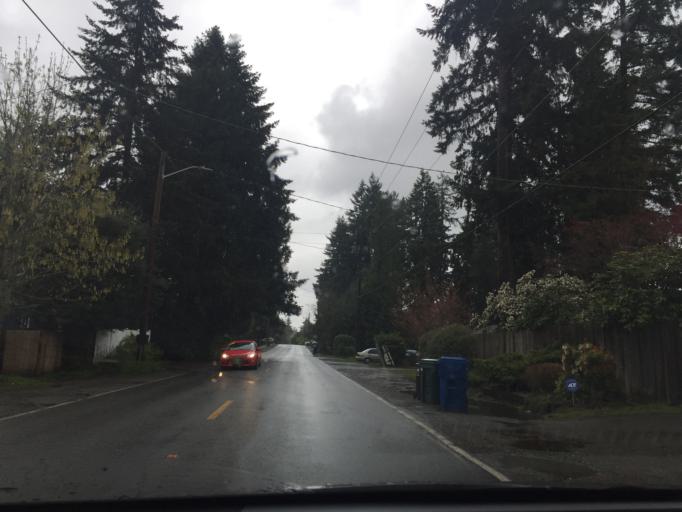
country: US
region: Washington
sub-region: King County
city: Lake Forest Park
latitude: 47.7281
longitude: -122.2964
